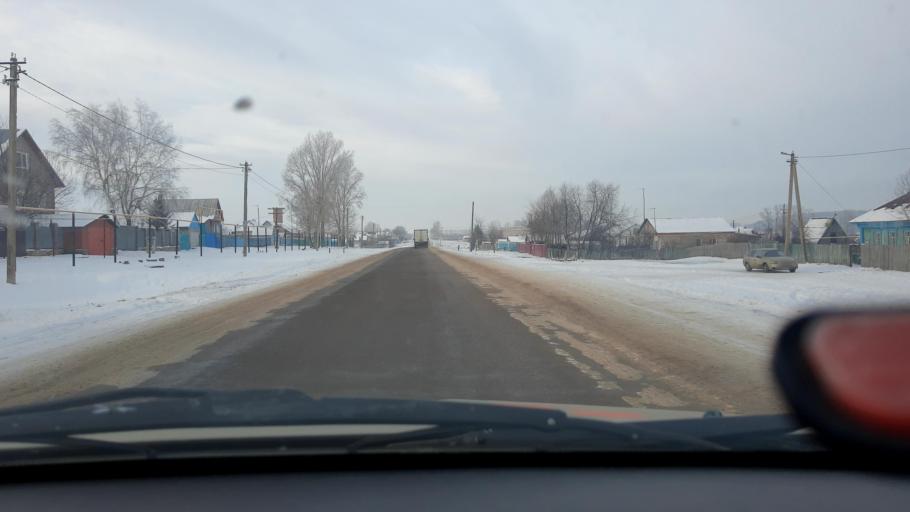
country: RU
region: Bashkortostan
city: Avdon
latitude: 54.3604
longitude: 55.8407
